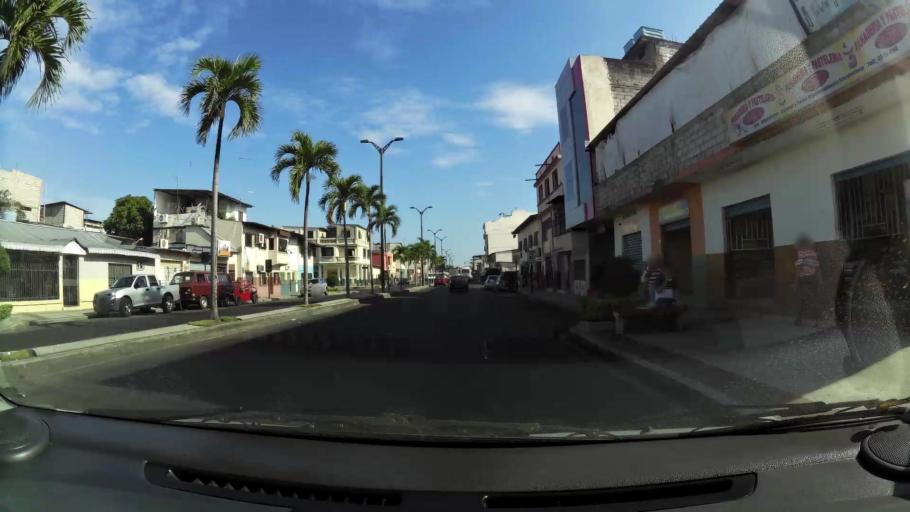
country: EC
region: Guayas
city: Guayaquil
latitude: -2.1996
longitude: -79.9156
